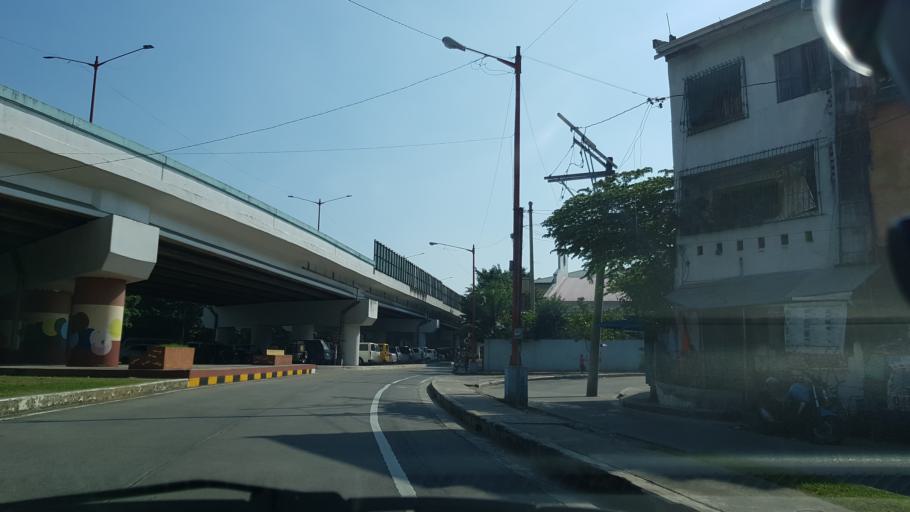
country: PH
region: Metro Manila
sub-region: Marikina
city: Calumpang
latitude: 14.6225
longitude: 121.0811
